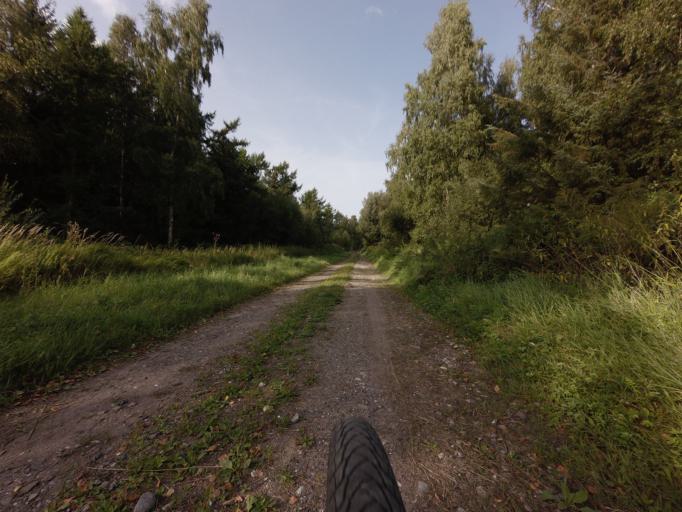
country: DK
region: Zealand
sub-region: Vordingborg Kommune
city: Praesto
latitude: 55.1432
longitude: 12.0967
